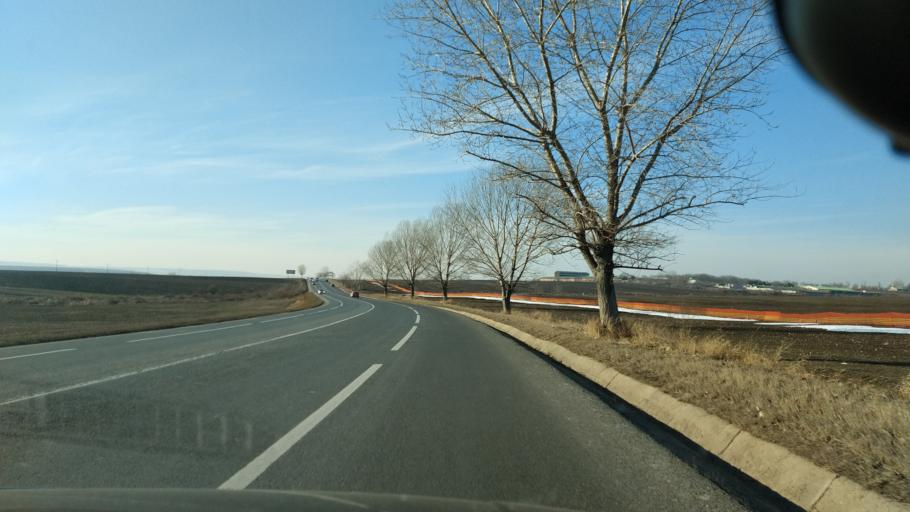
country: RO
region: Iasi
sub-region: Comuna Ion Neculce
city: Razboieni
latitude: 47.2218
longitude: 27.0850
